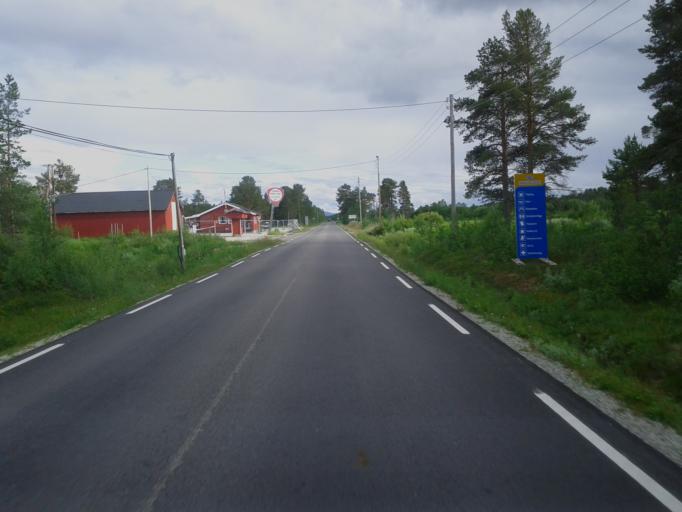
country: NO
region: Sor-Trondelag
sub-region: Roros
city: Roros
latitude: 62.2873
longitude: 11.7341
